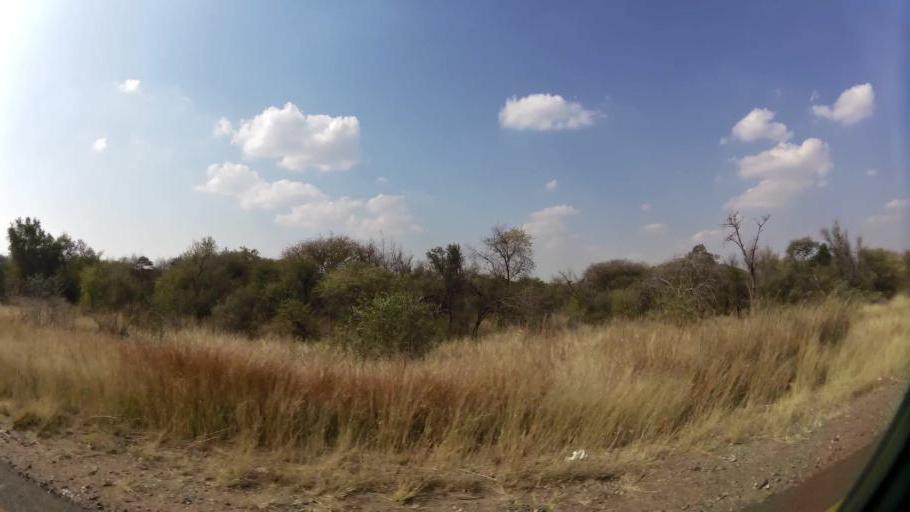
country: ZA
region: North-West
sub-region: Bojanala Platinum District Municipality
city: Mogwase
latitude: -25.4281
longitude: 27.0814
